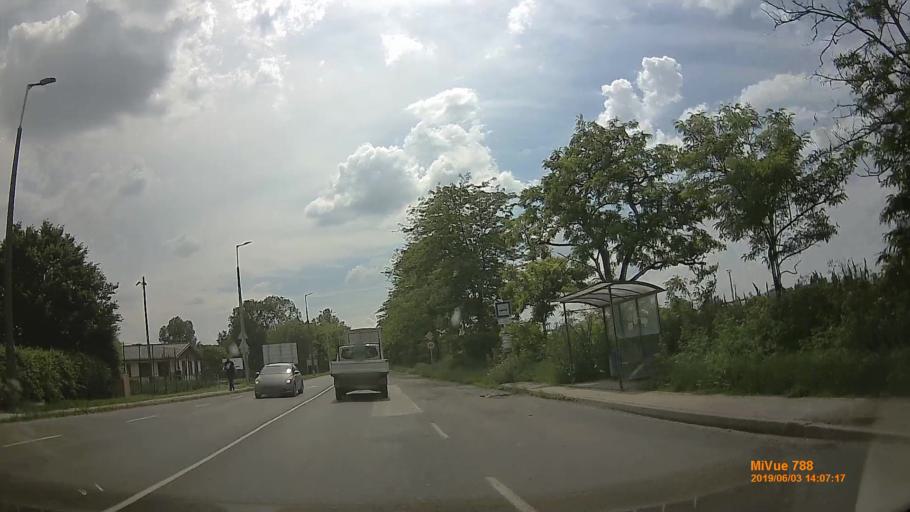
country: HU
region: Jasz-Nagykun-Szolnok
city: Toszeg
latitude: 47.1425
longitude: 20.1591
